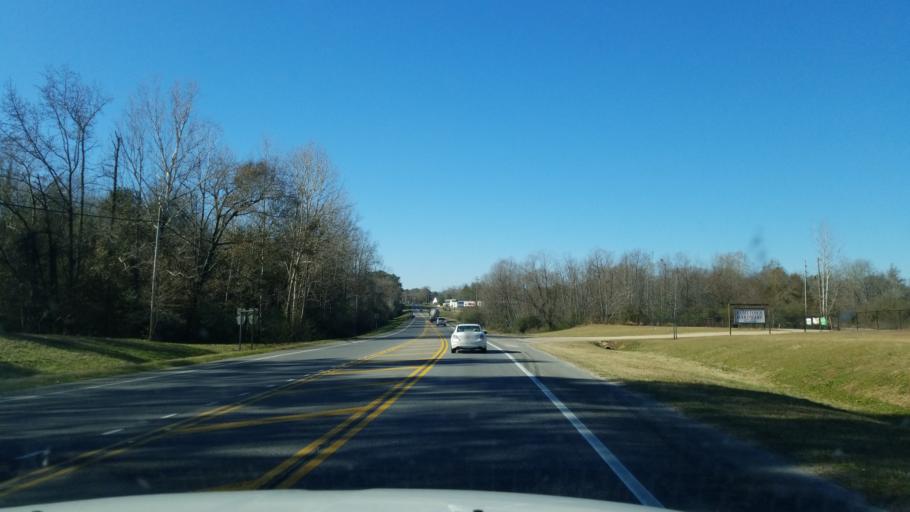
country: US
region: Alabama
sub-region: Pickens County
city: Gordo
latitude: 33.3139
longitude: -87.8953
